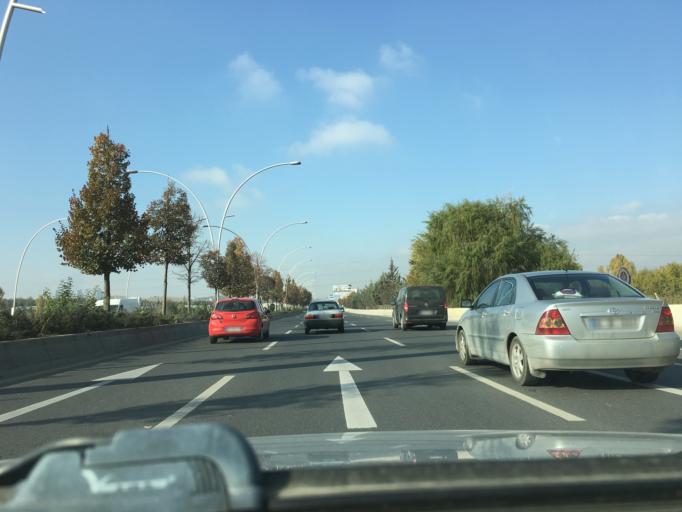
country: TR
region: Ankara
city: Batikent
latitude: 39.9069
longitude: 32.7389
